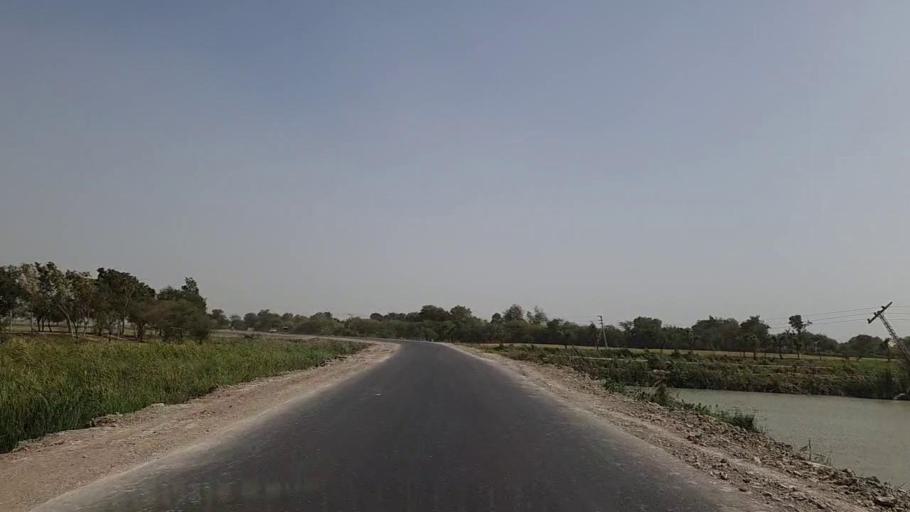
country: PK
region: Sindh
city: Tando Bago
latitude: 24.8105
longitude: 68.9143
